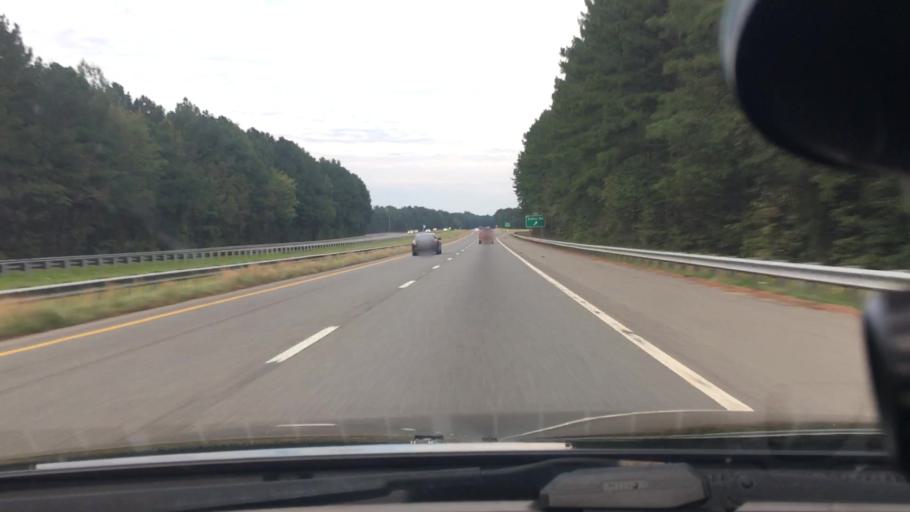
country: US
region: North Carolina
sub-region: Chatham County
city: Farmville
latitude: 35.5562
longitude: -79.1570
